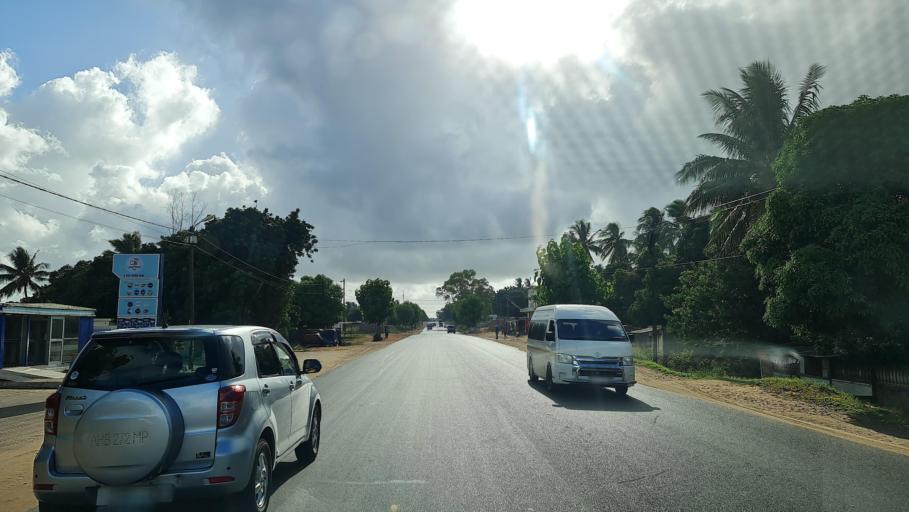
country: MZ
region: Gaza
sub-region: Xai-Xai District
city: Xai-Xai
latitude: -25.0565
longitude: 33.6853
